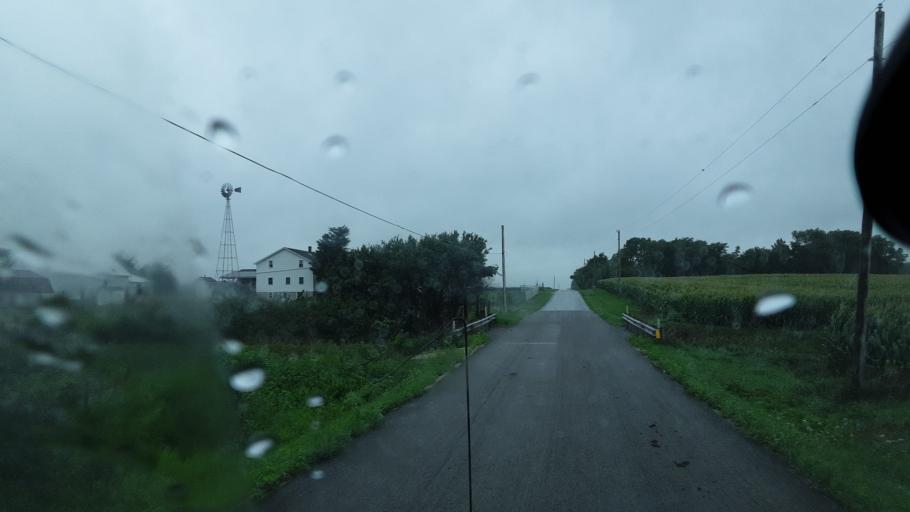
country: US
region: Ohio
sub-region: Mercer County
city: Rockford
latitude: 40.6847
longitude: -84.7947
